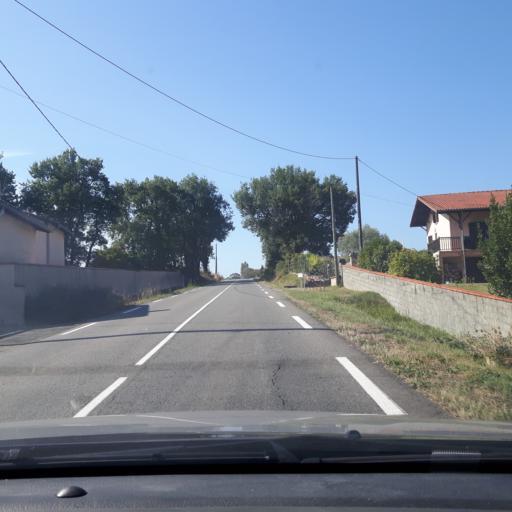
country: FR
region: Midi-Pyrenees
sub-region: Departement de la Haute-Garonne
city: Montjoire
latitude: 43.7647
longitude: 1.5280
